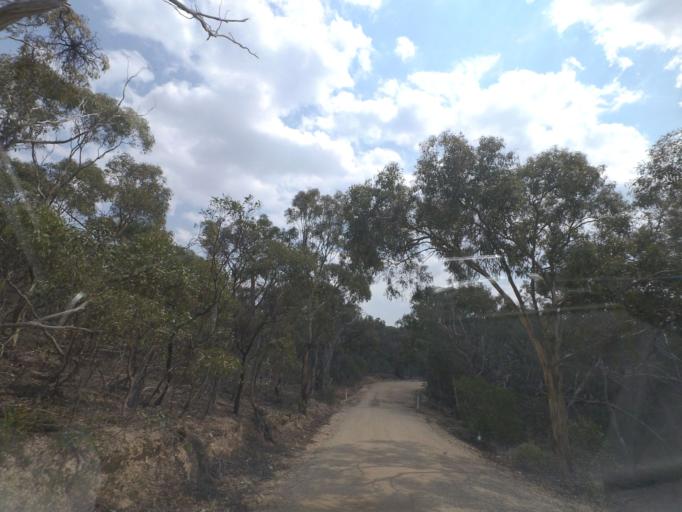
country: AU
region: Victoria
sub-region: Moorabool
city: Bacchus Marsh
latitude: -37.6089
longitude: 144.4446
